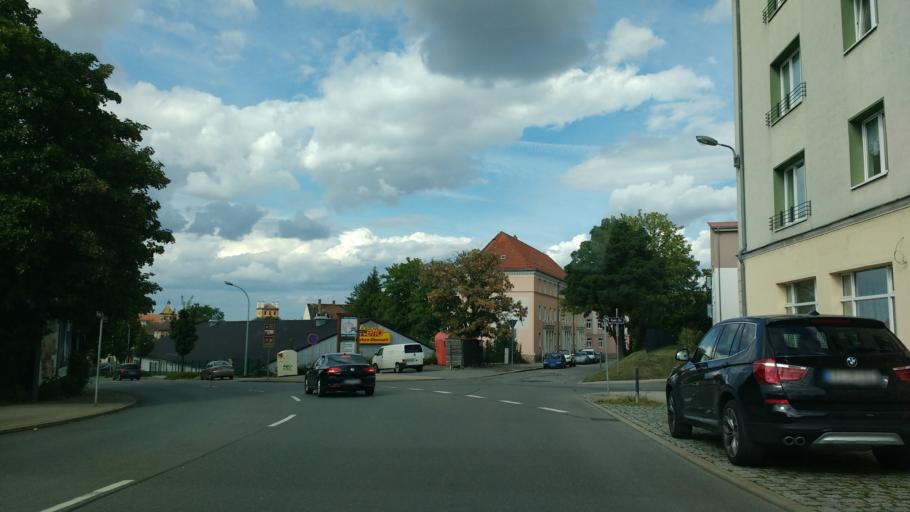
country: DE
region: Saxony-Anhalt
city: Zeitz
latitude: 51.0463
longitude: 12.1242
